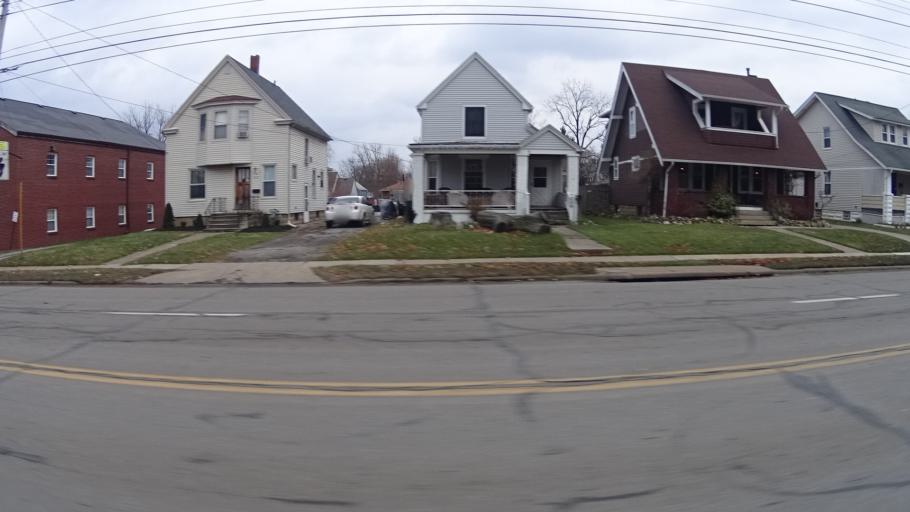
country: US
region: Ohio
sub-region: Lorain County
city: Elyria
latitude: 41.3747
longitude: -82.0944
